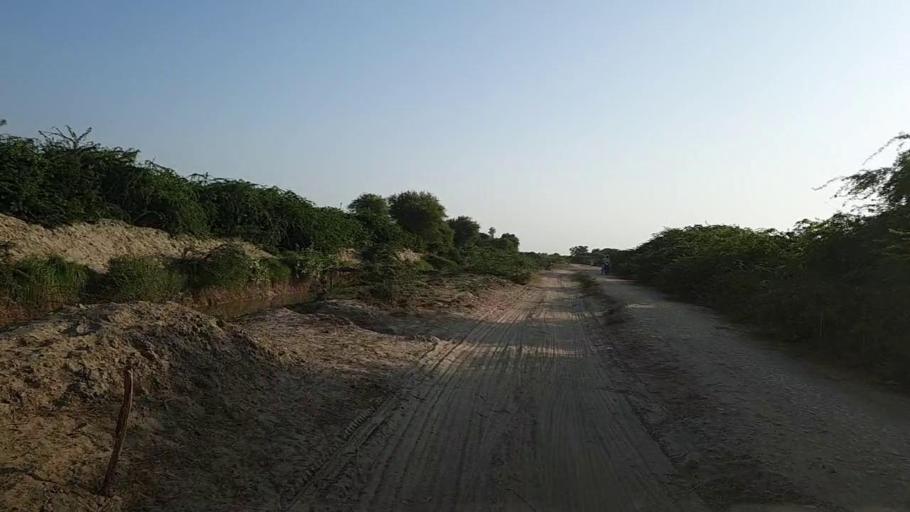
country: PK
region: Sindh
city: Kario
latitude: 24.7275
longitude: 68.6686
